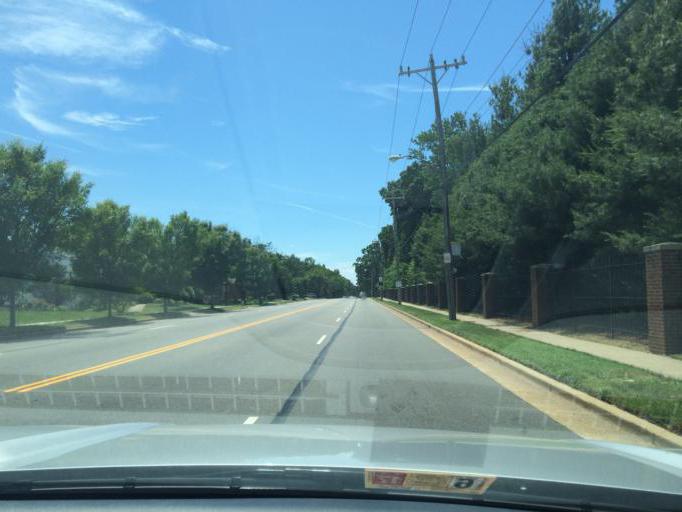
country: US
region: Virginia
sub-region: Fairfax County
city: Huntington
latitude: 38.8249
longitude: -77.0887
